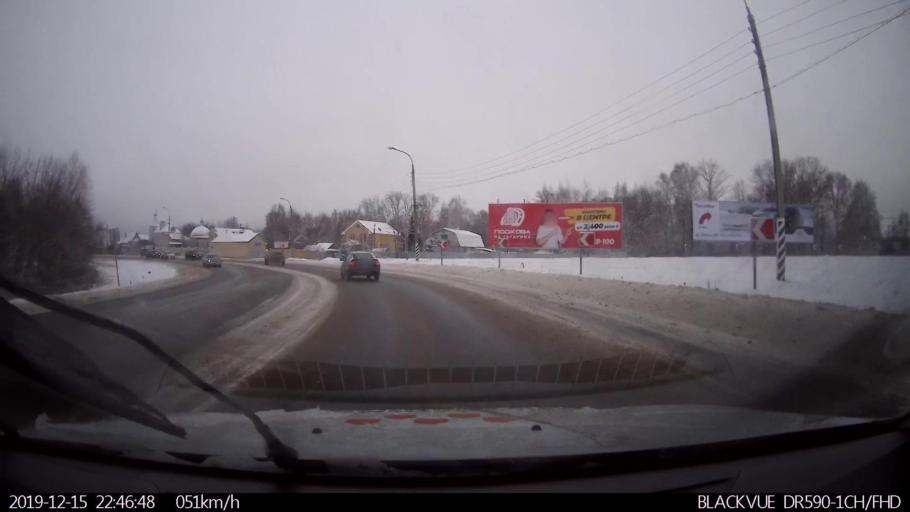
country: RU
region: Nizjnij Novgorod
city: Afonino
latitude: 56.2257
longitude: 44.0942
